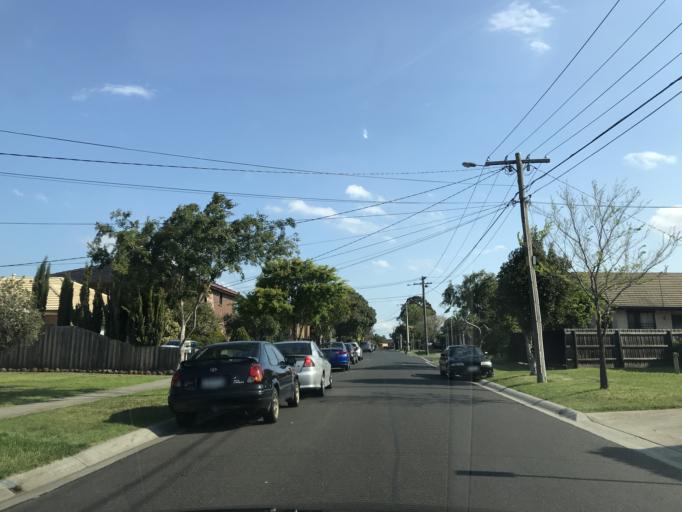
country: AU
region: Victoria
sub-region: Wyndham
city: Hoppers Crossing
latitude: -37.8813
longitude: 144.6997
